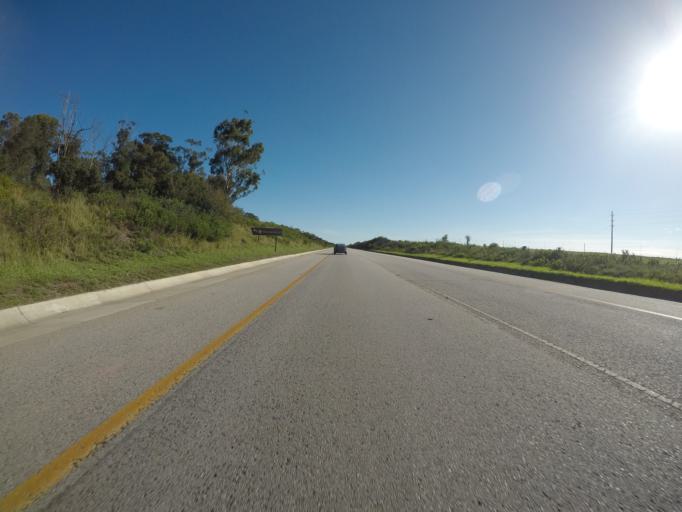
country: ZA
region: Eastern Cape
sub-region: Cacadu District Municipality
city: Jeffrey's Bay
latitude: -33.8927
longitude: 25.1334
